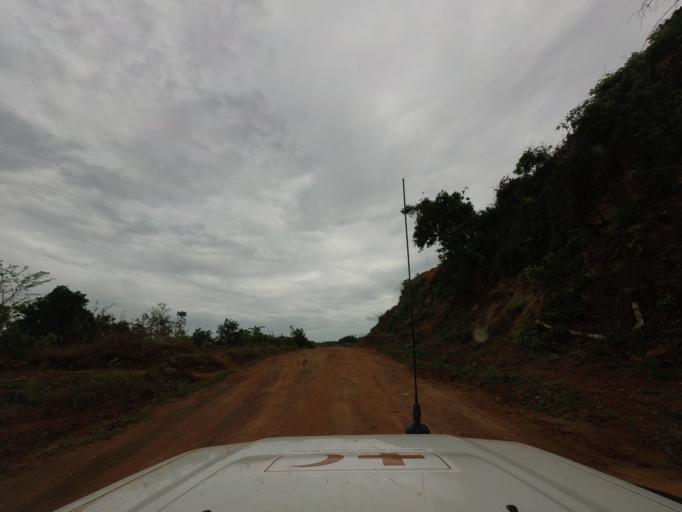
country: LR
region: Nimba
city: Sanniquellie
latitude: 7.2842
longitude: -8.8228
